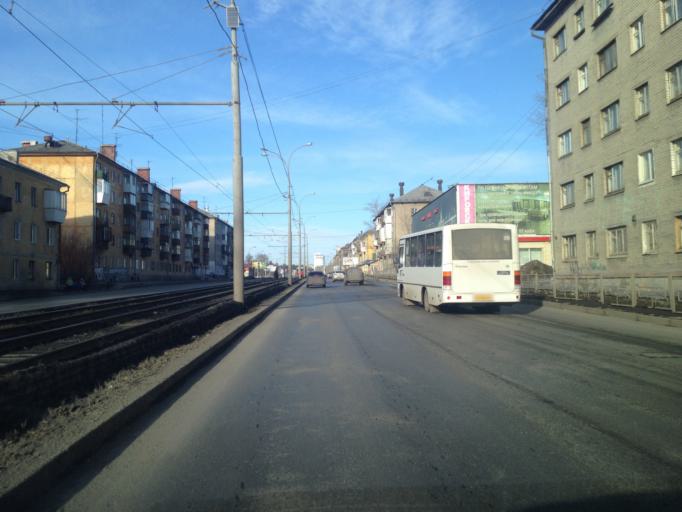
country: RU
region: Sverdlovsk
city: Yekaterinburg
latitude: 56.8860
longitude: 60.5646
